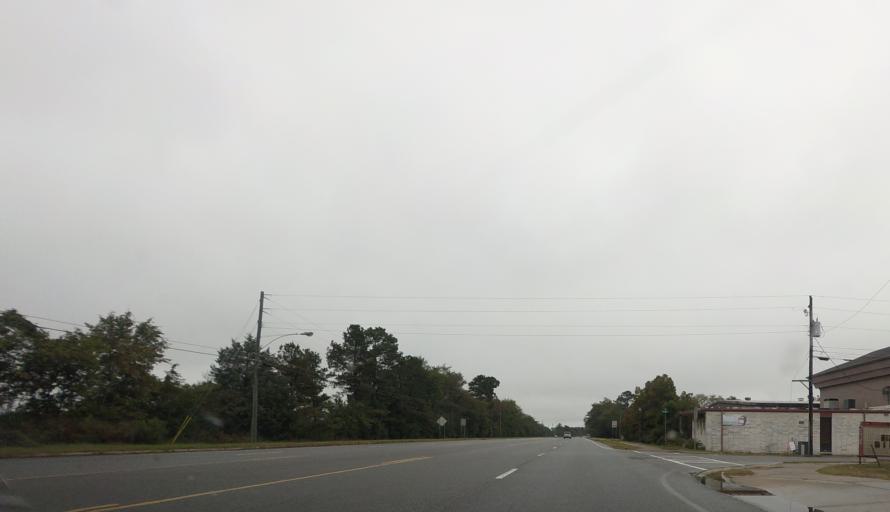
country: US
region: Georgia
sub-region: Taylor County
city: Reynolds
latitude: 32.5587
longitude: -84.0891
